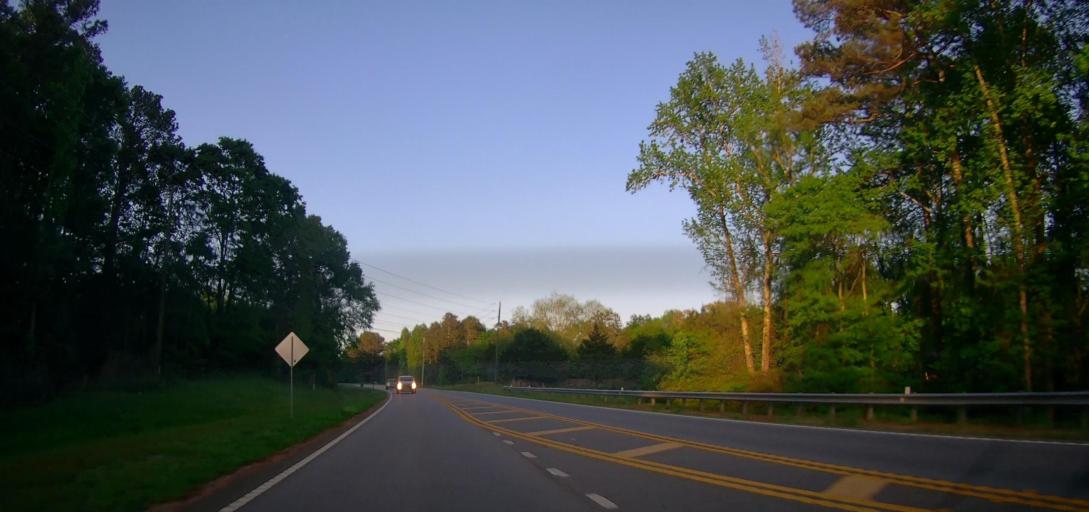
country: US
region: Georgia
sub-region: Newton County
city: Oakwood
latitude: 33.4415
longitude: -83.9975
